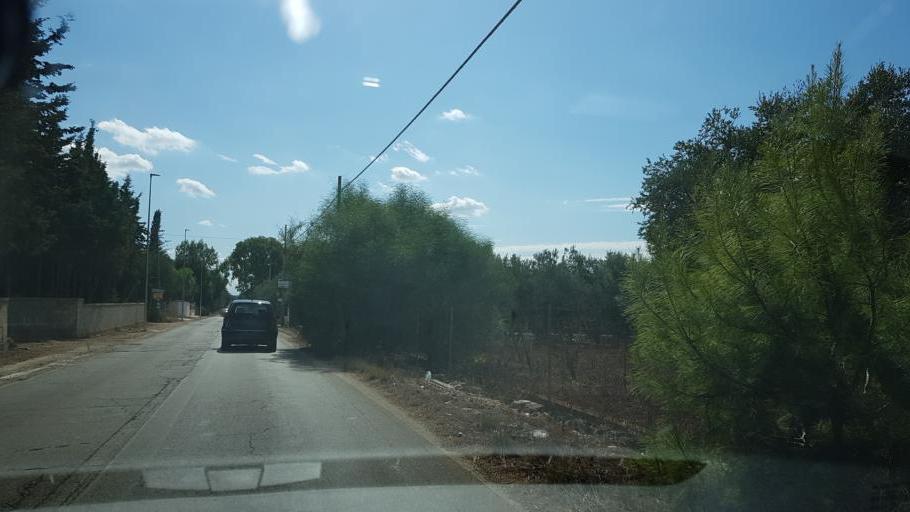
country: IT
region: Apulia
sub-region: Provincia di Lecce
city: Porto Cesareo
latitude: 40.2372
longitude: 17.9172
